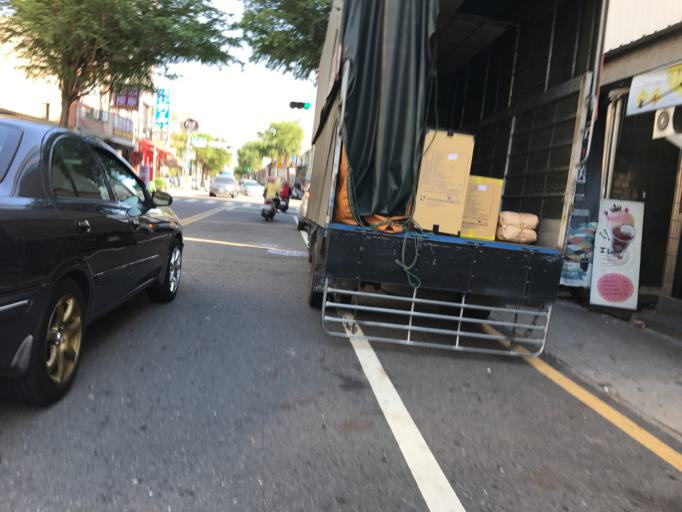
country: TW
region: Taiwan
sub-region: Tainan
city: Tainan
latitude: 22.9997
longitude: 120.1641
